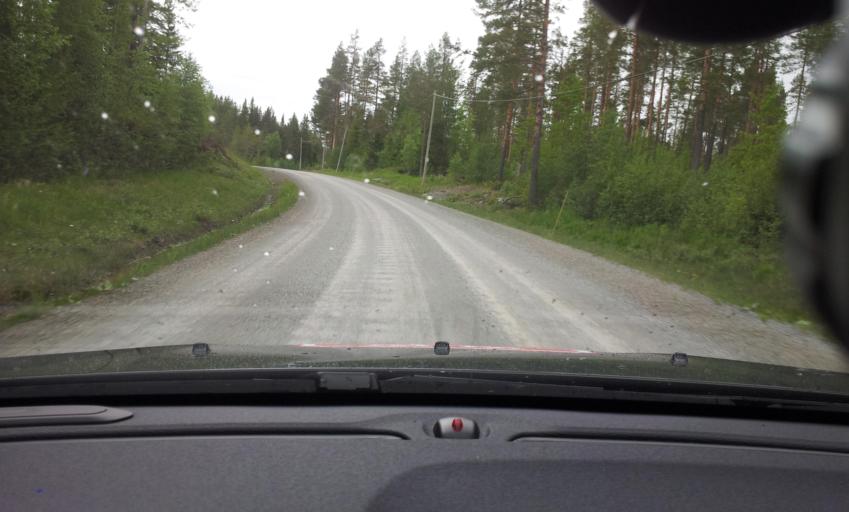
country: SE
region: Jaemtland
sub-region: OEstersunds Kommun
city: Brunflo
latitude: 63.1053
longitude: 15.0453
